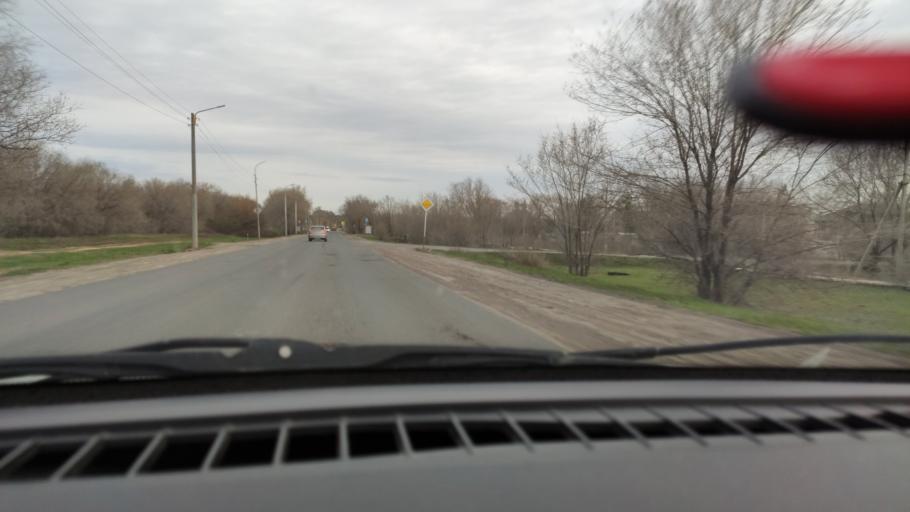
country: RU
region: Orenburg
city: Tatarskaya Kargala
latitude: 51.8730
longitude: 55.1454
